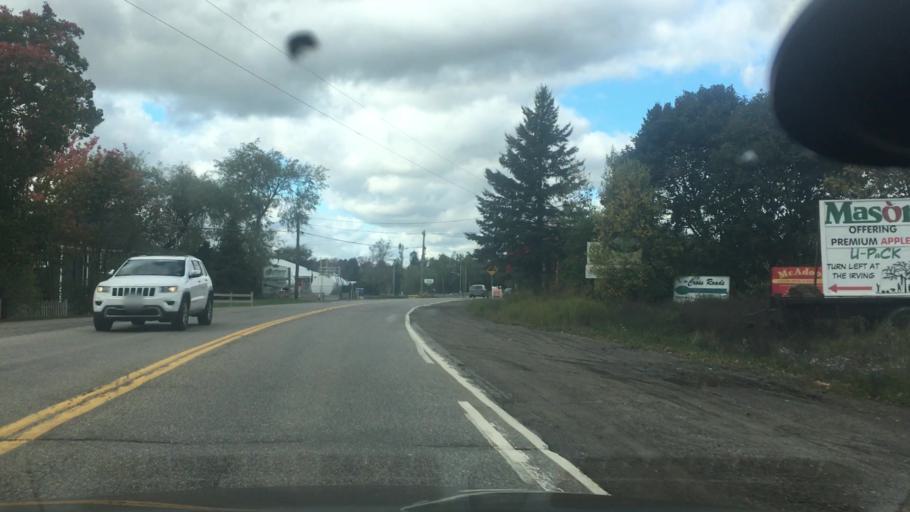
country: CA
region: Nova Scotia
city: Windsor
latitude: 44.9737
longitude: -64.1021
